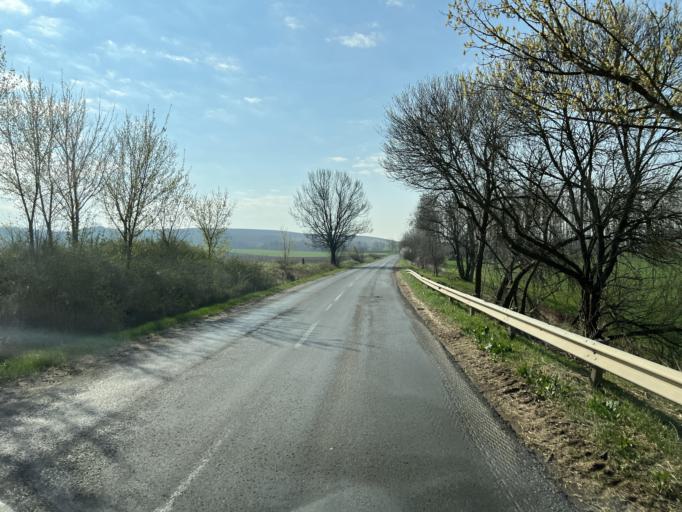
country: HU
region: Pest
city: Galgamacsa
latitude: 47.7305
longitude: 19.3756
